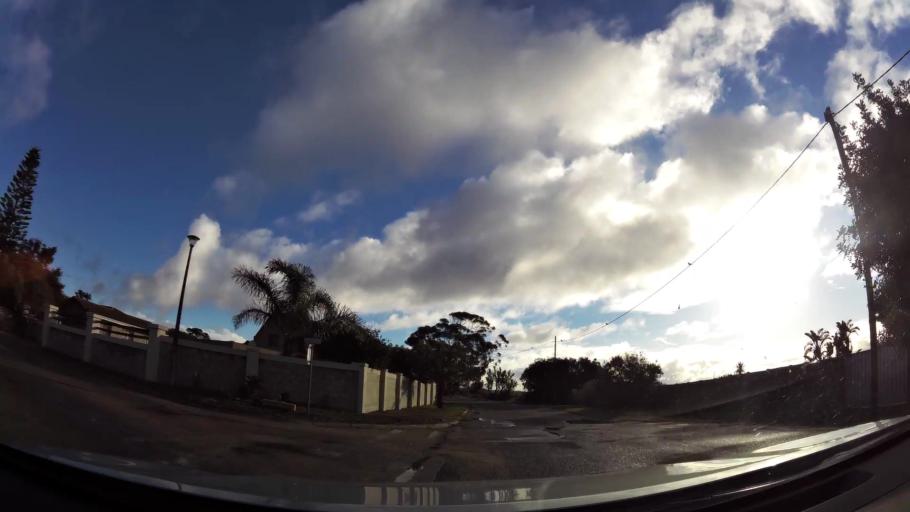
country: ZA
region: Western Cape
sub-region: Eden District Municipality
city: Riversdale
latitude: -34.2085
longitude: 21.5812
